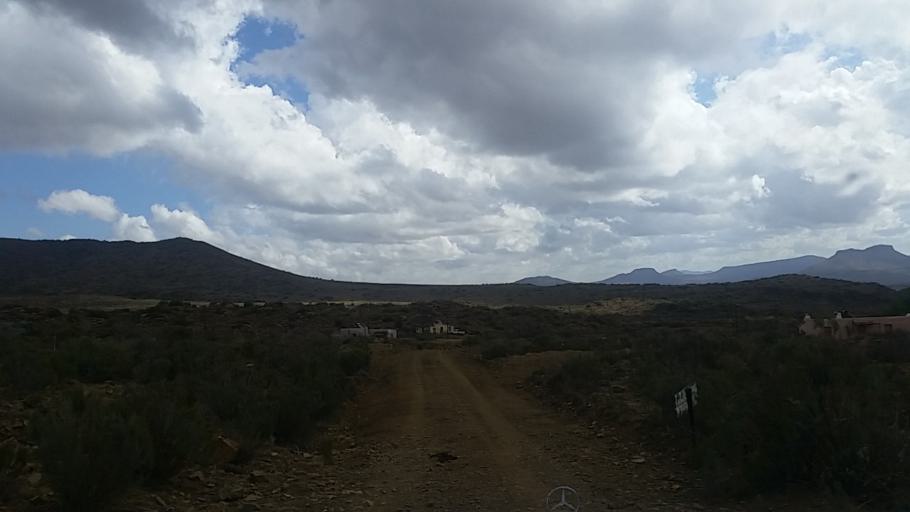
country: ZA
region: Eastern Cape
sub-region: Chris Hani District Municipality
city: Middelburg
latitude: -31.7914
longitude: 24.6623
